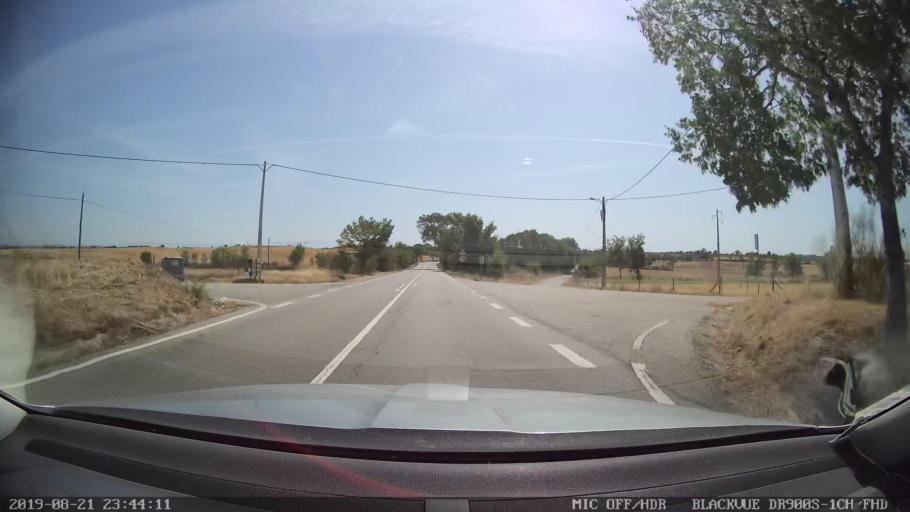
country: PT
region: Castelo Branco
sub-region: Idanha-A-Nova
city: Idanha-a-Nova
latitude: 39.8471
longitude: -7.2824
